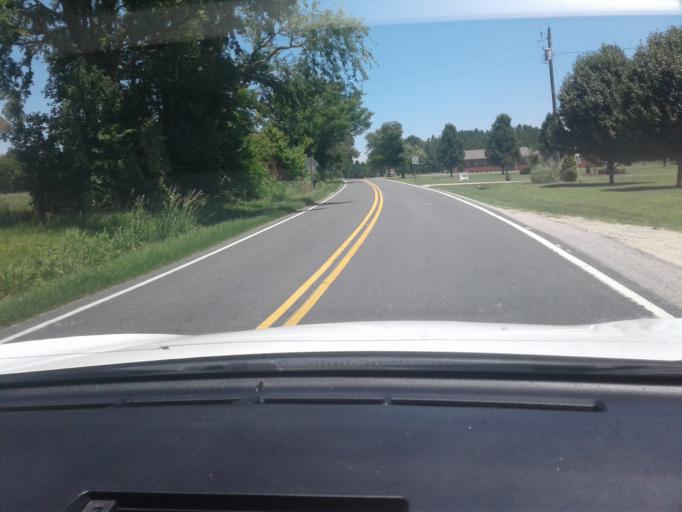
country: US
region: North Carolina
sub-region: Harnett County
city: Lillington
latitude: 35.3894
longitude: -78.7940
